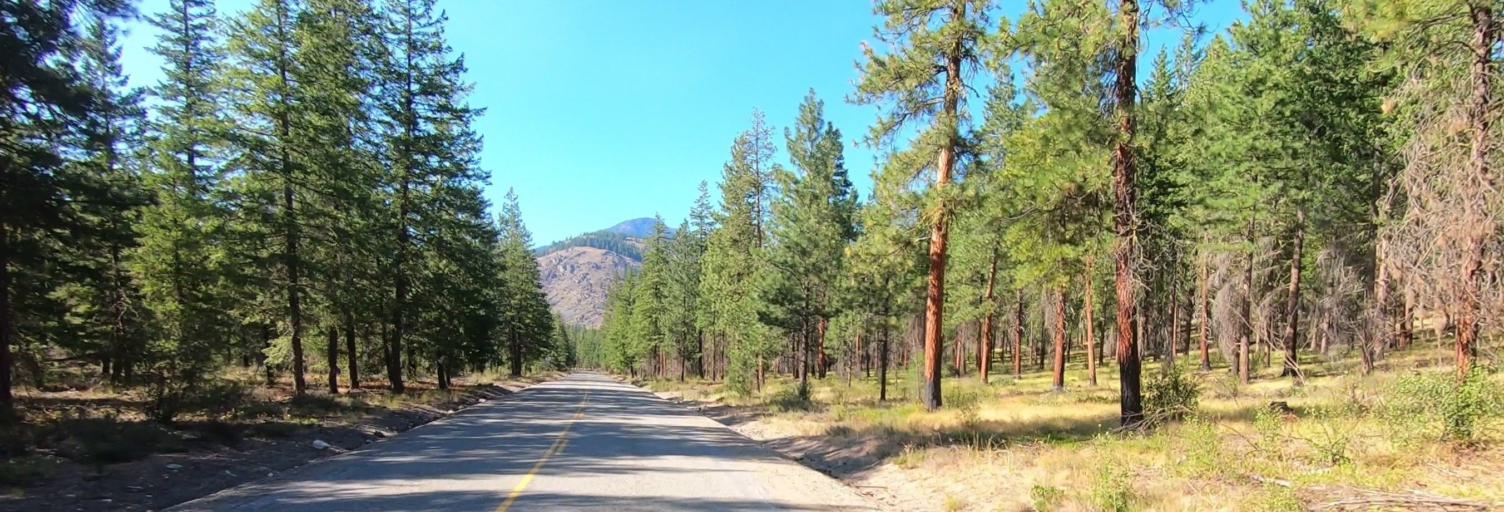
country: US
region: Washington
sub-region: Chelan County
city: Granite Falls
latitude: 48.5727
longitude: -120.3661
